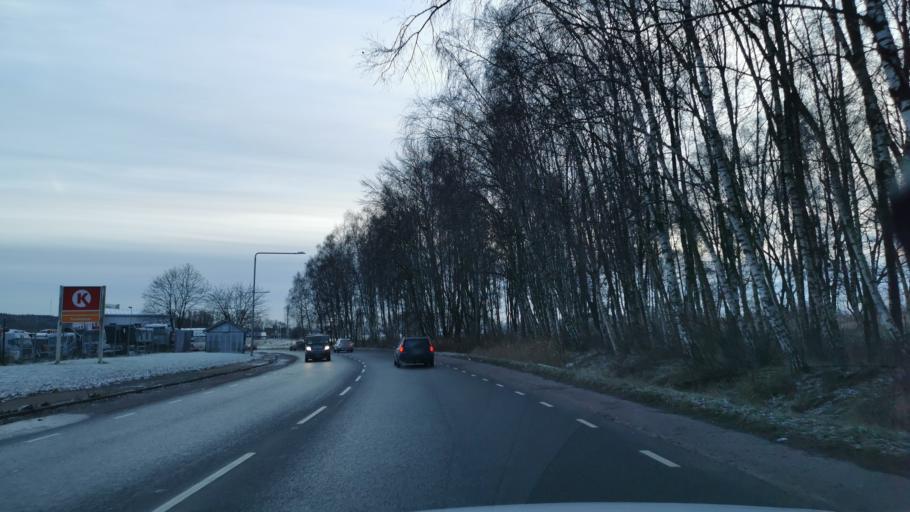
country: SE
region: Vaestra Goetaland
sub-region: Goteborg
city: Hammarkullen
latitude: 57.7621
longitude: 11.9938
